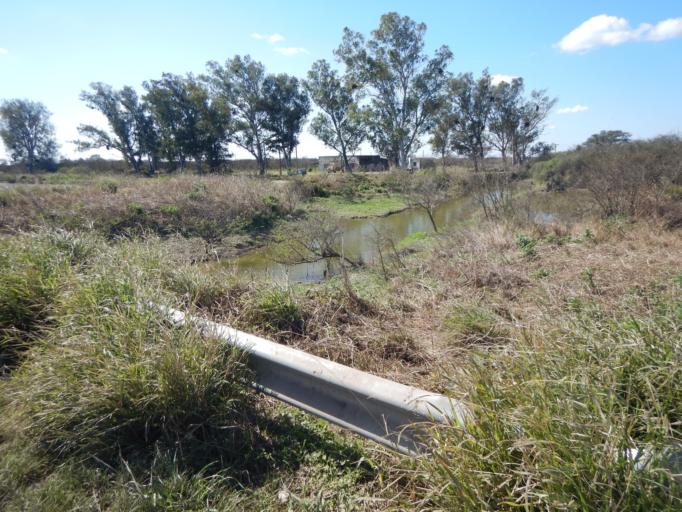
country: AR
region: Santa Fe
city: Tostado
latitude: -28.6750
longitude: -61.5313
